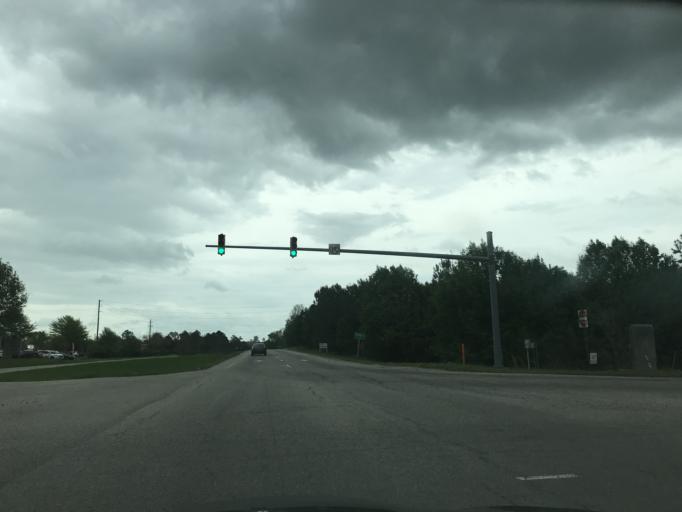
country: US
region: North Carolina
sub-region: Wake County
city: Knightdale
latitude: 35.8038
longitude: -78.4244
